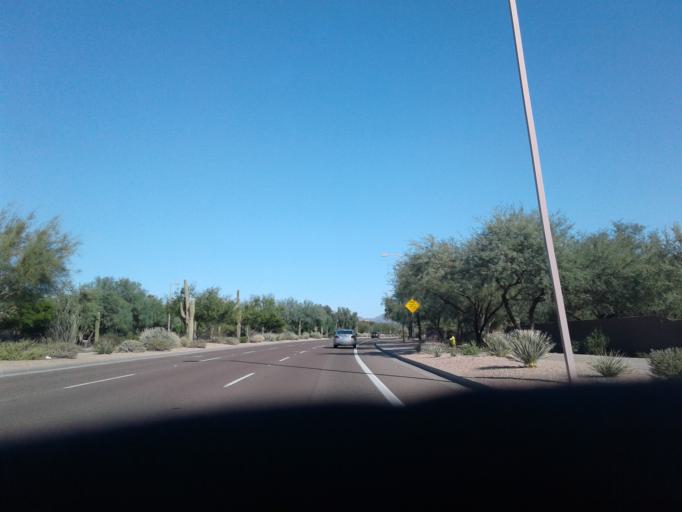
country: US
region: Arizona
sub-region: Maricopa County
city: Cave Creek
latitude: 33.6863
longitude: -111.9935
